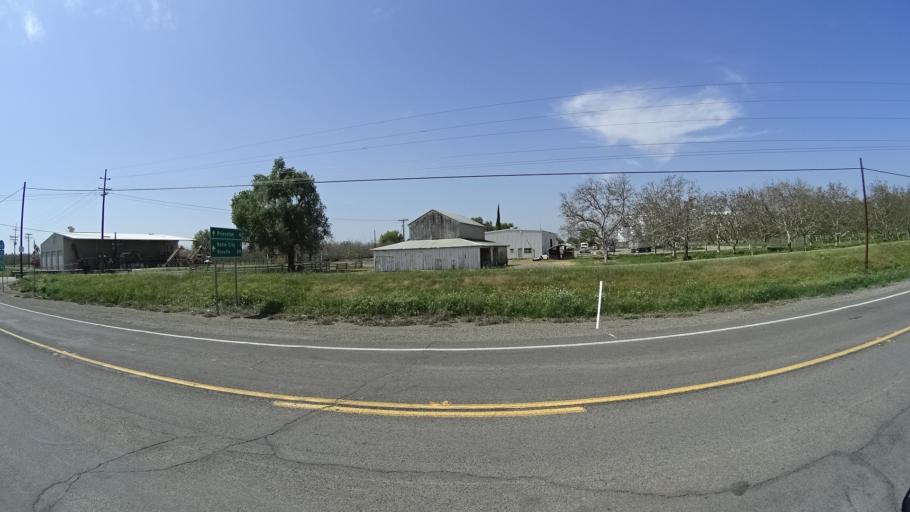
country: US
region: California
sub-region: Glenn County
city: Willows
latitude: 39.4578
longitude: -122.0173
